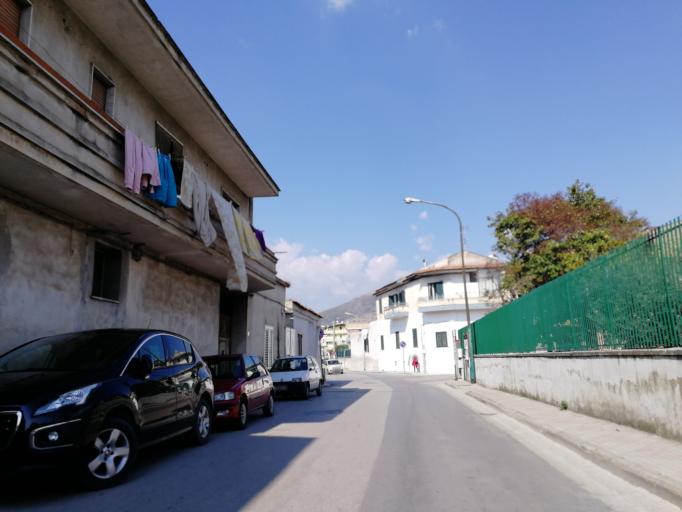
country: IT
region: Campania
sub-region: Provincia di Caserta
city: San Prisco
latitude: 41.0875
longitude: 14.2737
